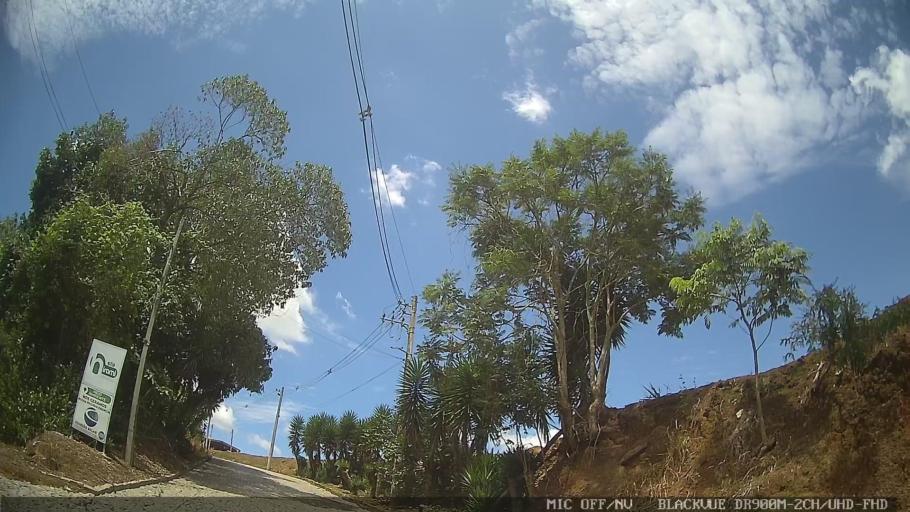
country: BR
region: Sao Paulo
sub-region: Biritiba-Mirim
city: Biritiba Mirim
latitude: -23.6019
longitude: -46.0532
